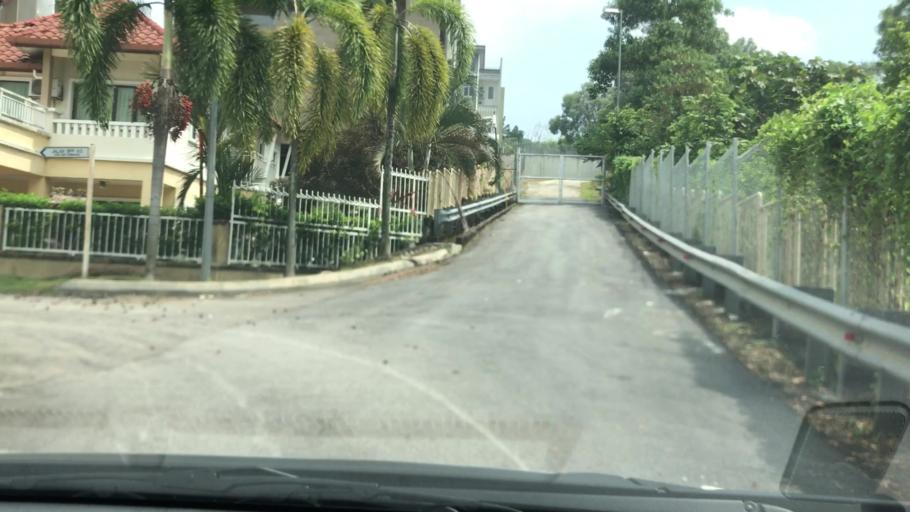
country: MY
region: Putrajaya
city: Putrajaya
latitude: 2.9890
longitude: 101.6683
